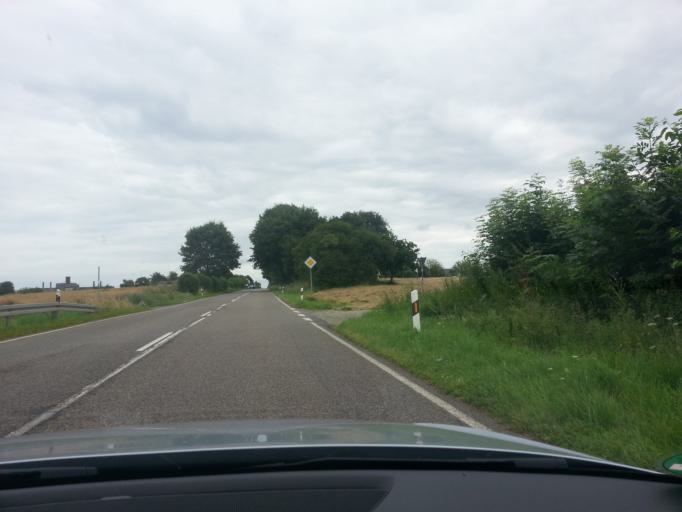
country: DE
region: Rheinland-Pfalz
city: Kirf
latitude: 49.4863
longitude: 6.4560
